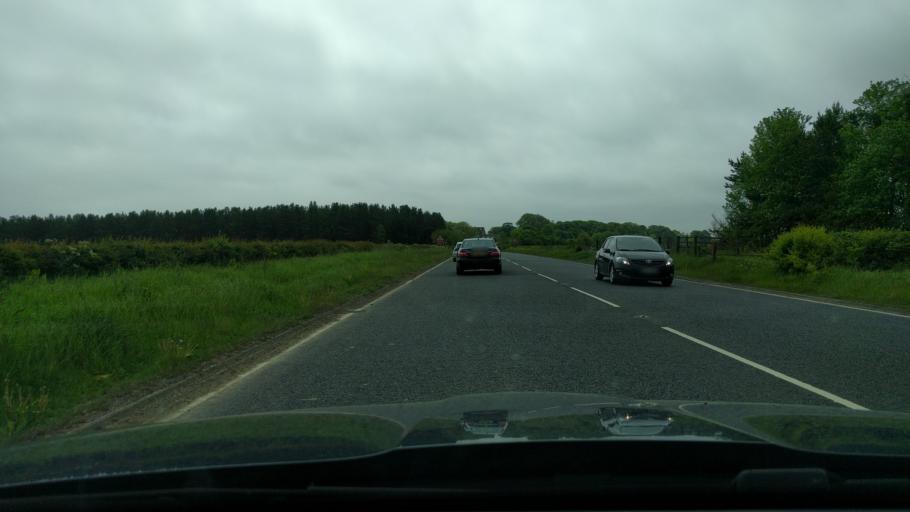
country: GB
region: England
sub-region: Northumberland
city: East Chevington
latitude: 55.2605
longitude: -1.6038
